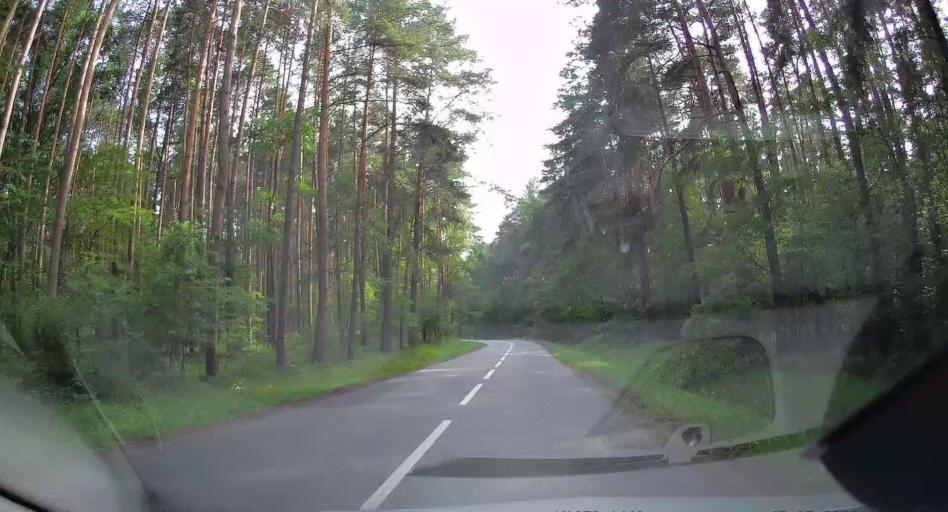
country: PL
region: Lodz Voivodeship
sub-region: Powiat tomaszowski
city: Inowlodz
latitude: 51.5460
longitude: 20.2377
